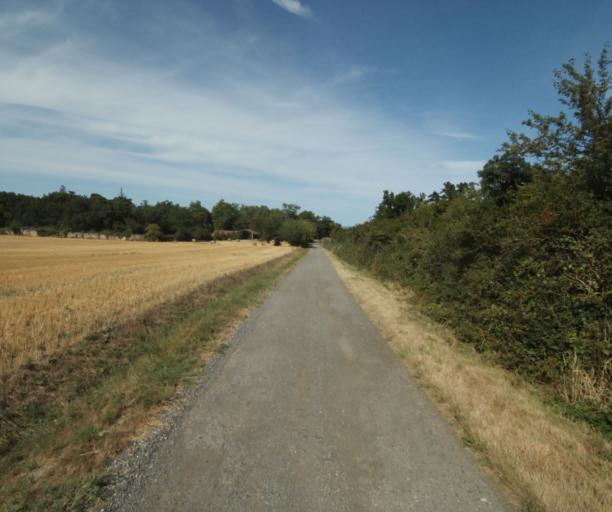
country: FR
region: Midi-Pyrenees
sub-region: Departement du Tarn
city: Soual
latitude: 43.5178
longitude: 2.0918
